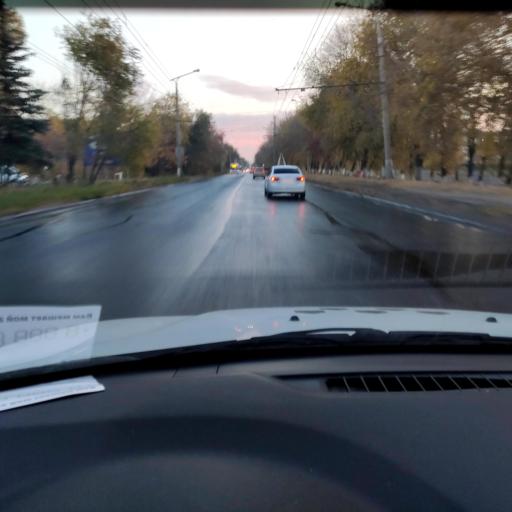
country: RU
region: Samara
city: Tol'yatti
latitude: 53.5373
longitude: 49.4415
